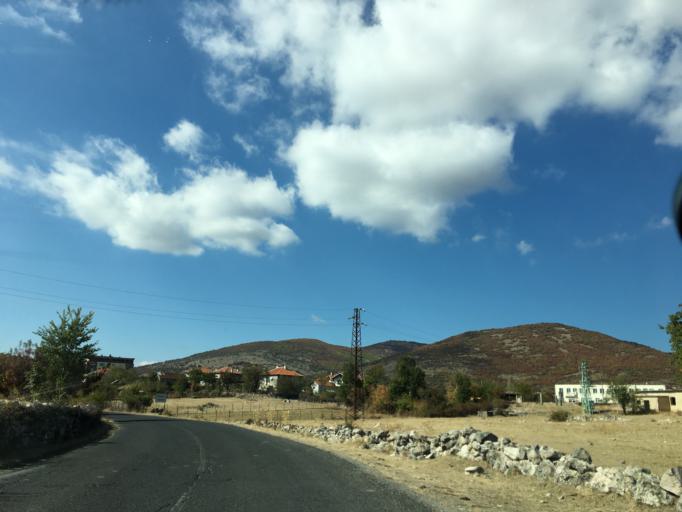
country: BG
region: Kurdzhali
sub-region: Obshtina Kurdzhali
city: Kurdzhali
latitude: 41.5453
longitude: 25.4961
